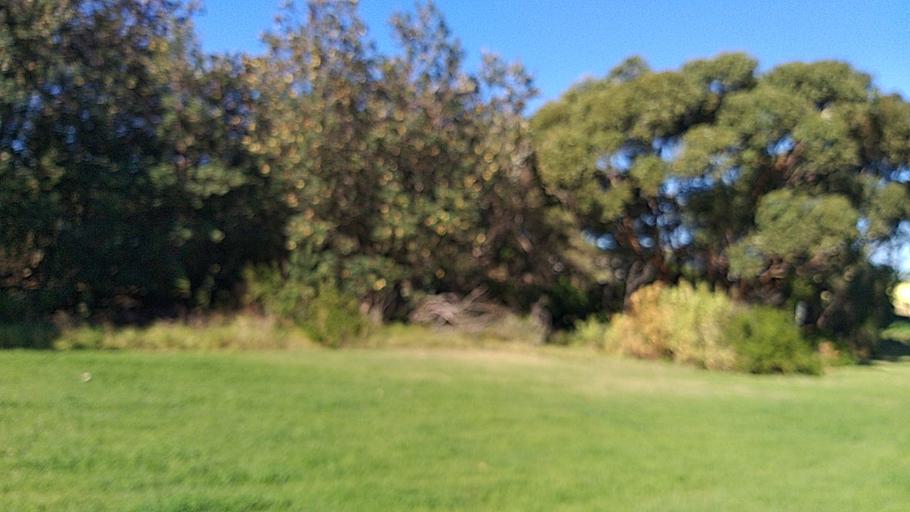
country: AU
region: New South Wales
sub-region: Wollongong
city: Corrimal
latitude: -34.3881
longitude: 150.9092
